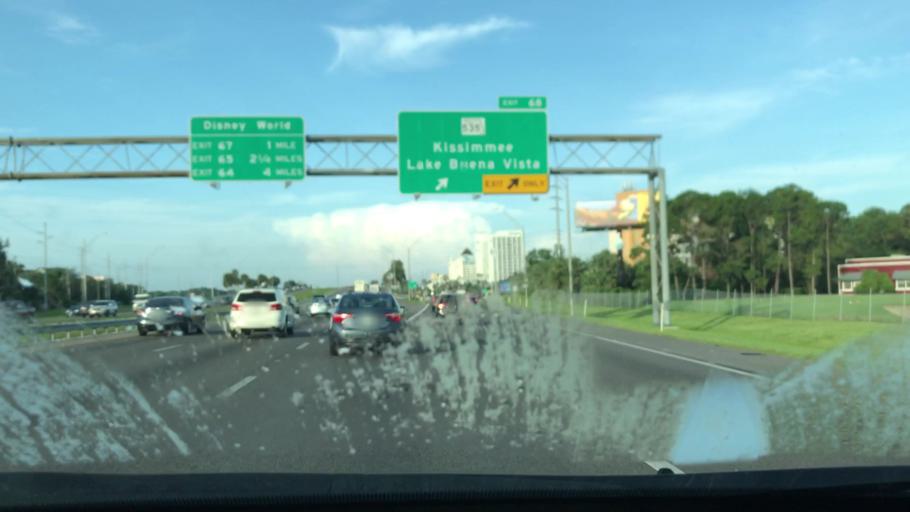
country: US
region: Florida
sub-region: Osceola County
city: Celebration
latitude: 28.3810
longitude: -81.5022
